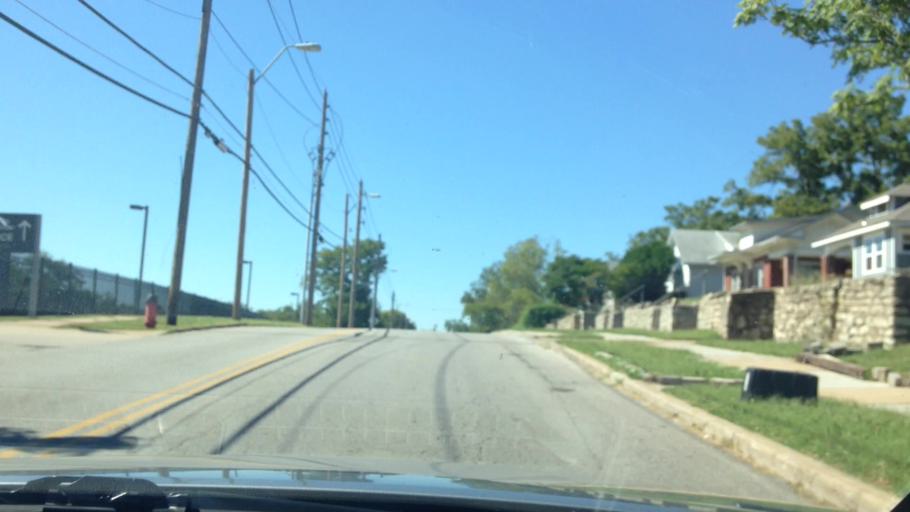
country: US
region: Kansas
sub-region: Johnson County
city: Mission Hills
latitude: 39.0189
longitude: -94.5429
